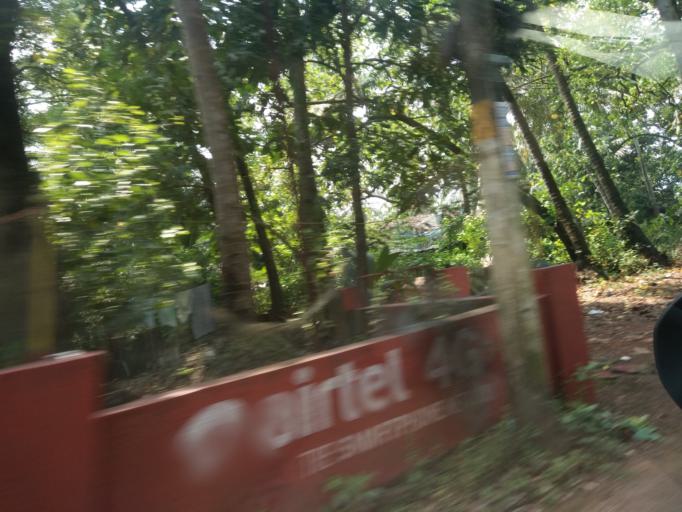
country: IN
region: Goa
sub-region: North Goa
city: Goa Velha
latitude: 15.4408
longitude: 73.8693
